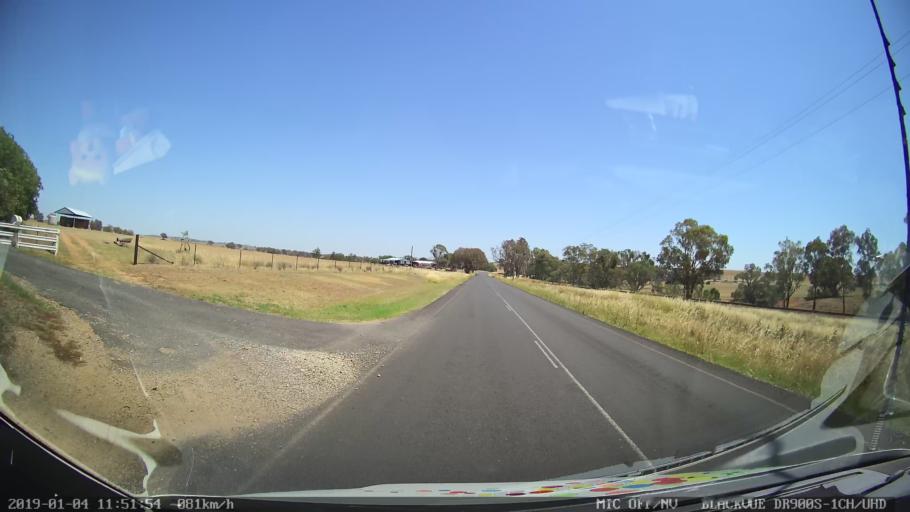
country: AU
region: New South Wales
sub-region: Cabonne
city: Molong
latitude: -32.8898
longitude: 148.7524
